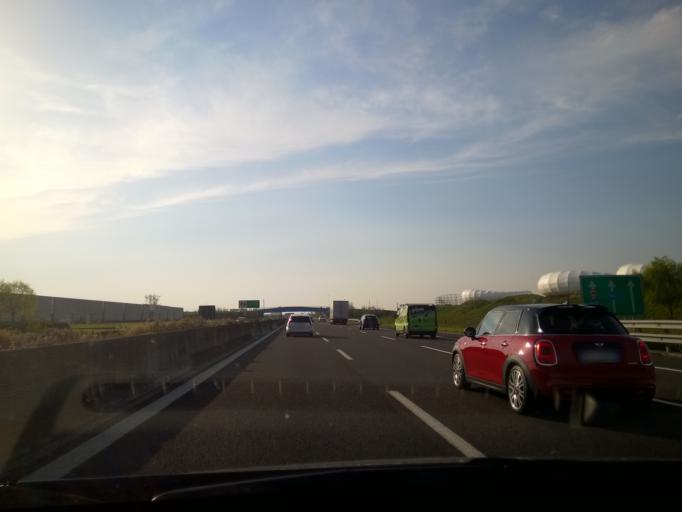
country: IT
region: Emilia-Romagna
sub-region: Provincia di Ravenna
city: Faenza
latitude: 44.3267
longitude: 11.8977
